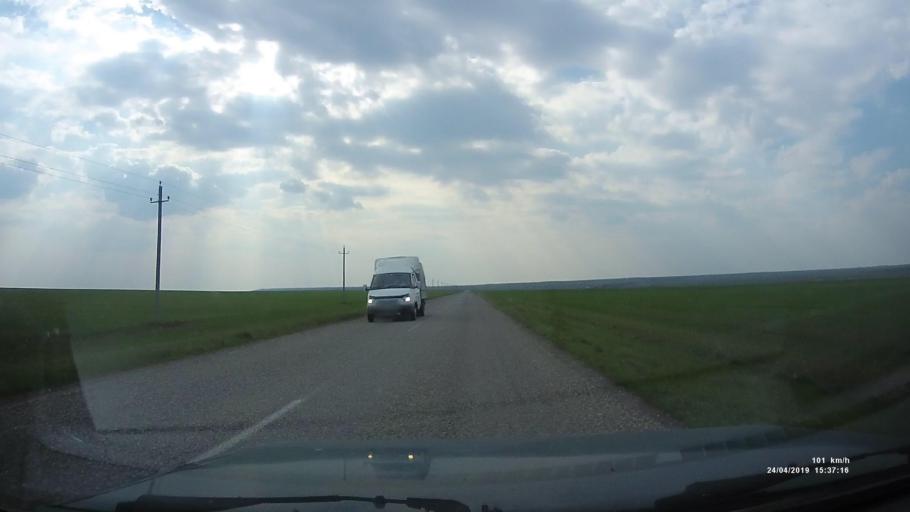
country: RU
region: Kalmykiya
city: Yashalta
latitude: 46.5995
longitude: 42.8527
